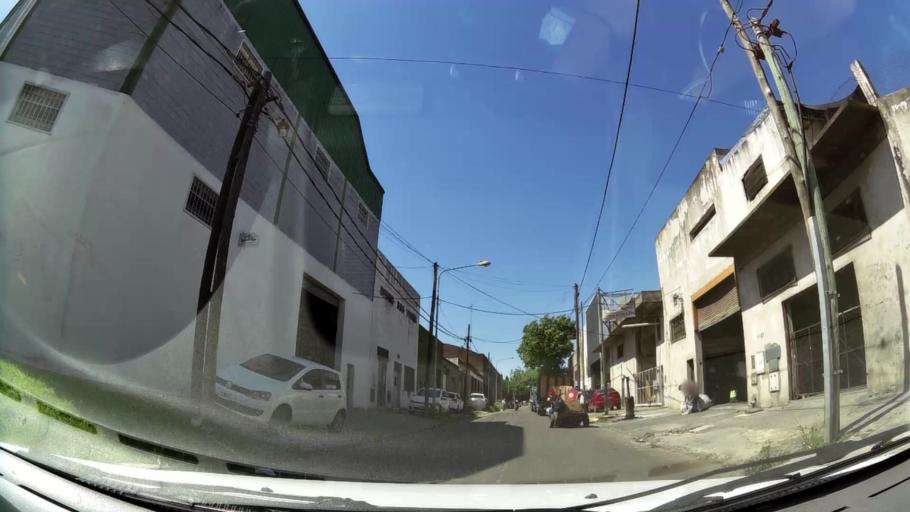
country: AR
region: Buenos Aires
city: Caseros
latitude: -34.5737
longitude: -58.5536
